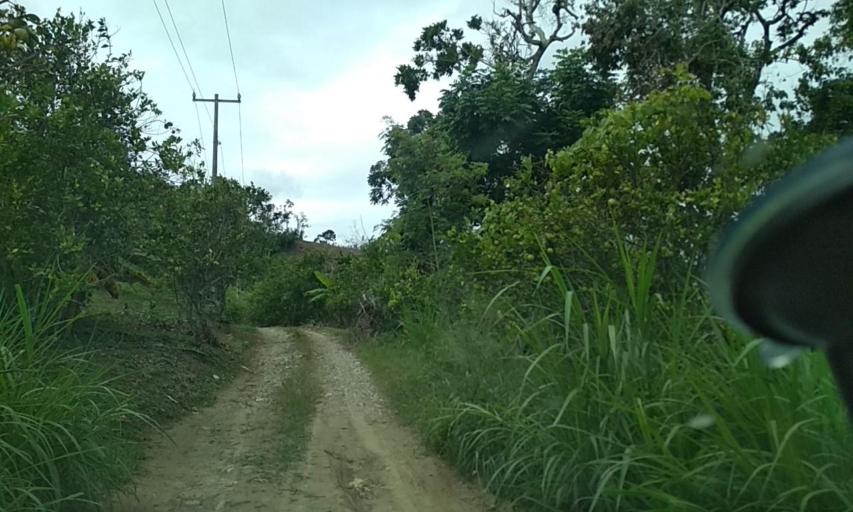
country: MX
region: Veracruz
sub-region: Papantla
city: Residencial Tajin
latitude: 20.6163
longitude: -97.3522
